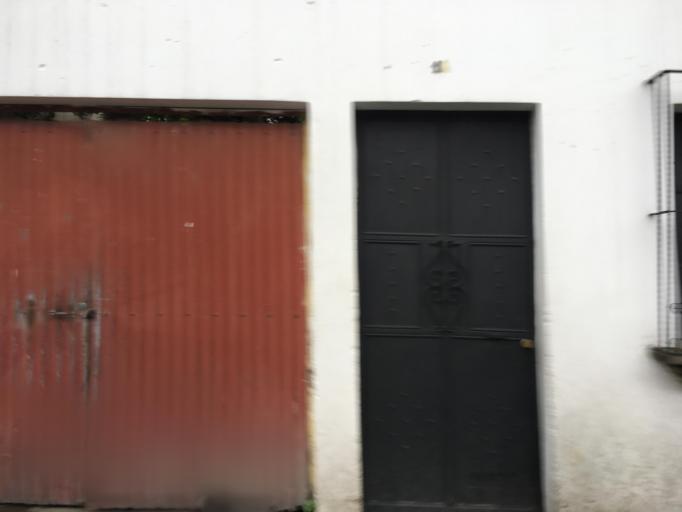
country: GT
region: Sacatepequez
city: Antigua Guatemala
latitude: 14.5644
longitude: -90.7406
